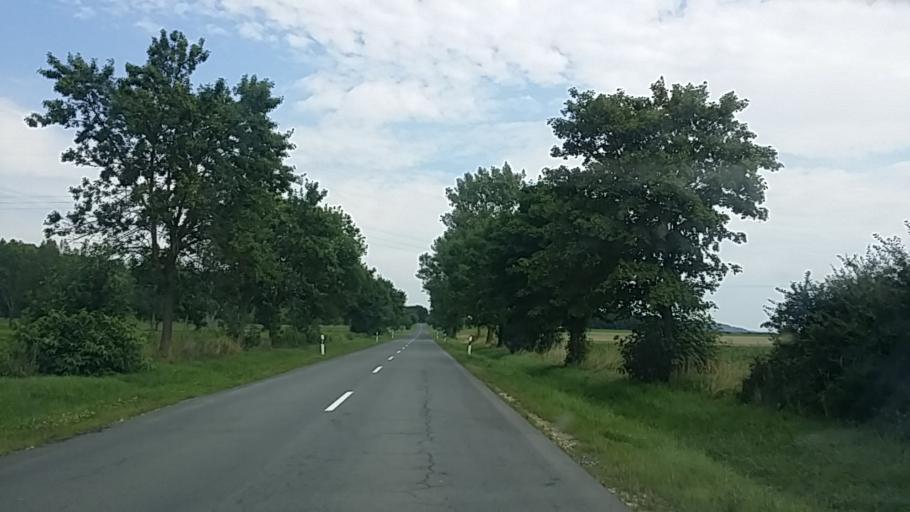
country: HR
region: Medimurska
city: Podturen
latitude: 46.5152
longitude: 16.5903
